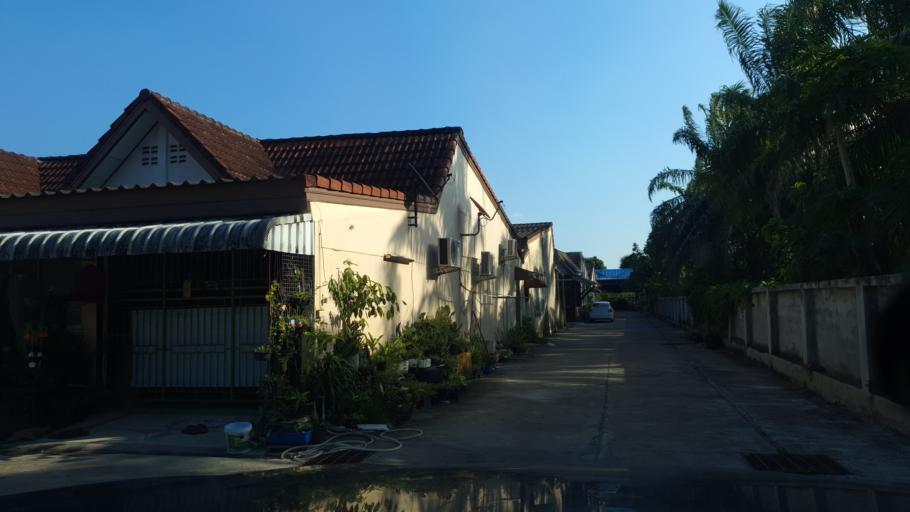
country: TH
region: Krabi
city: Nuea Khlong
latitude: 8.0825
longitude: 98.9881
